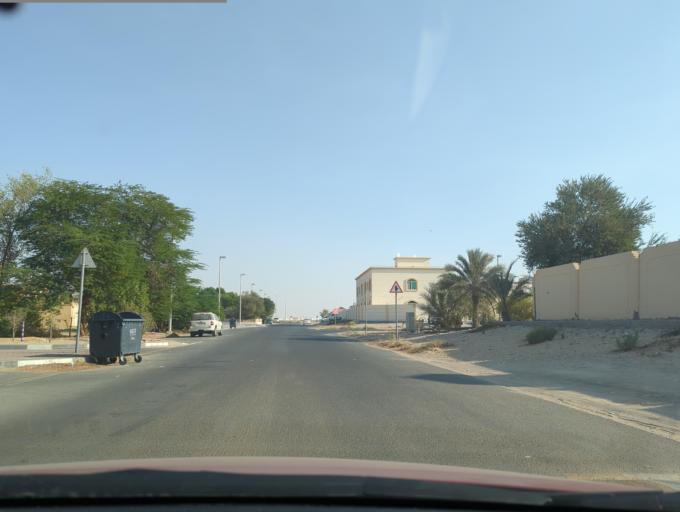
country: AE
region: Abu Dhabi
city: Abu Dhabi
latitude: 24.3972
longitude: 54.7428
